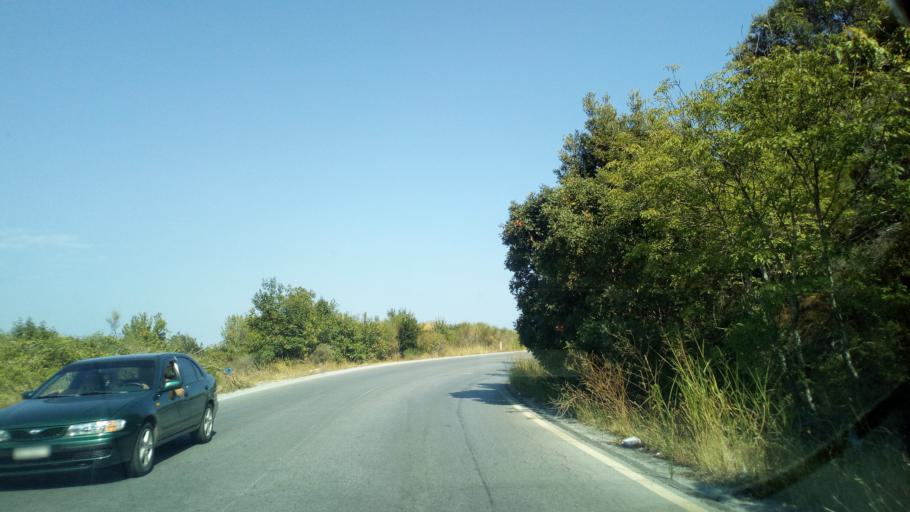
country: GR
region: Central Macedonia
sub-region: Nomos Thessalonikis
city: Stavros
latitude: 40.6552
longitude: 23.7389
